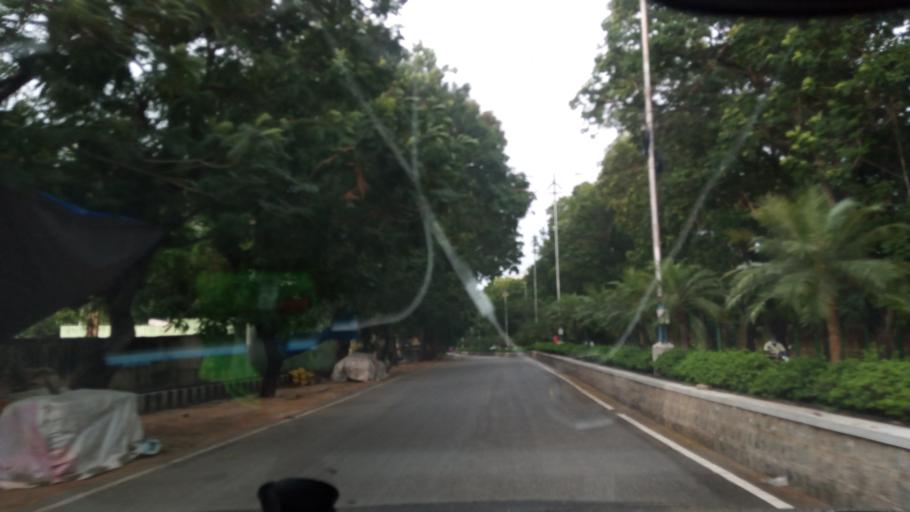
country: IN
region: Andhra Pradesh
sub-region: Chittoor
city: Akkarampalle
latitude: 13.6459
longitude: 79.4098
